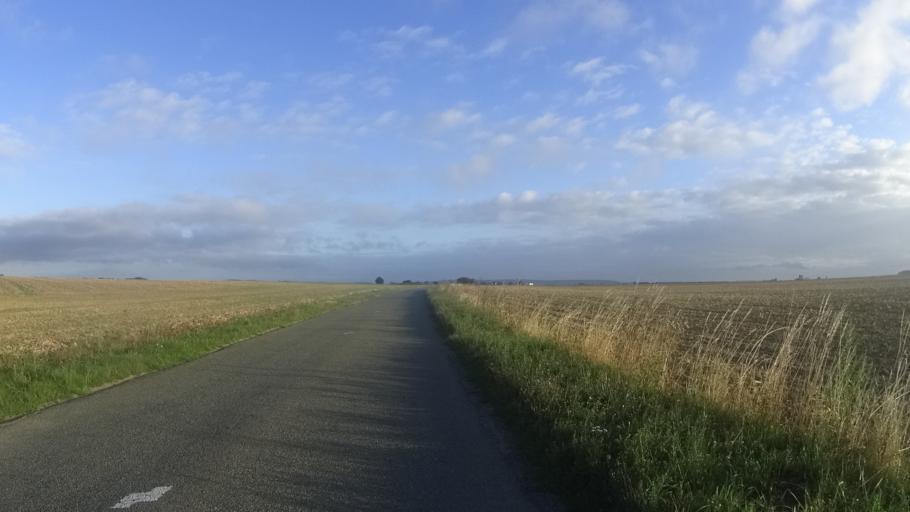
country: FR
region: Picardie
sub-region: Departement de l'Oise
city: Chamant
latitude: 49.1938
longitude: 2.6693
